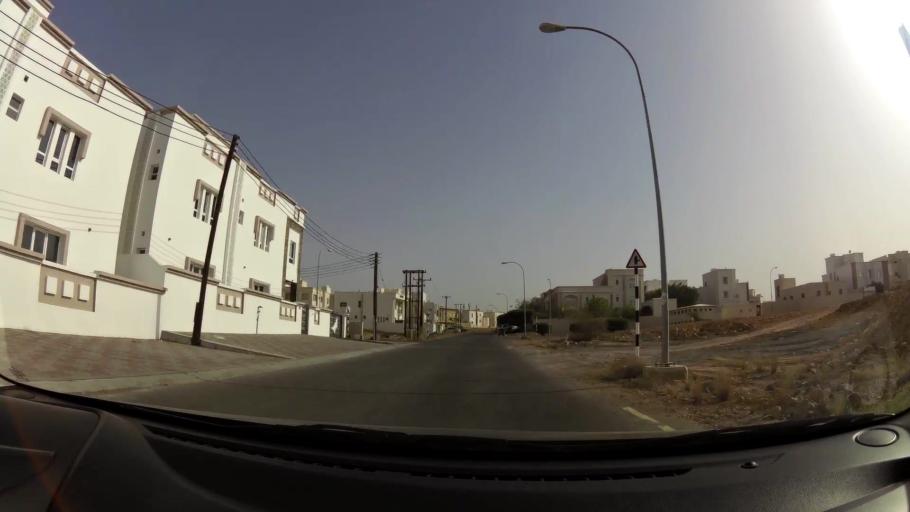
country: OM
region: Muhafazat Masqat
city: Bawshar
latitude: 23.5557
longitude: 58.3626
